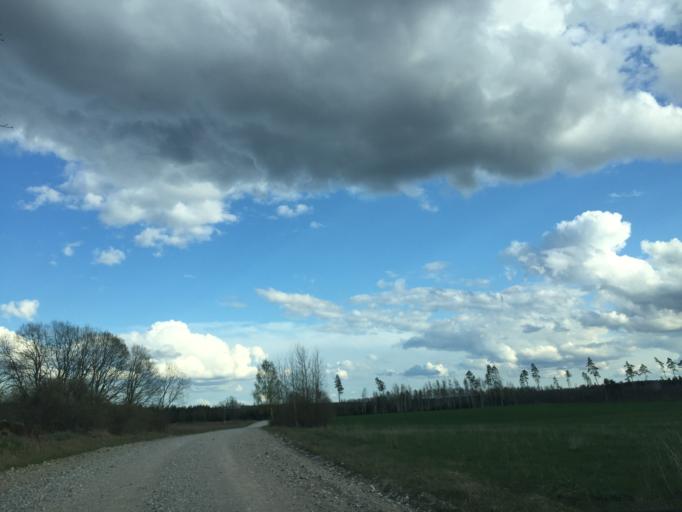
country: LV
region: Raunas
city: Rauna
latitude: 57.3689
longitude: 25.5092
